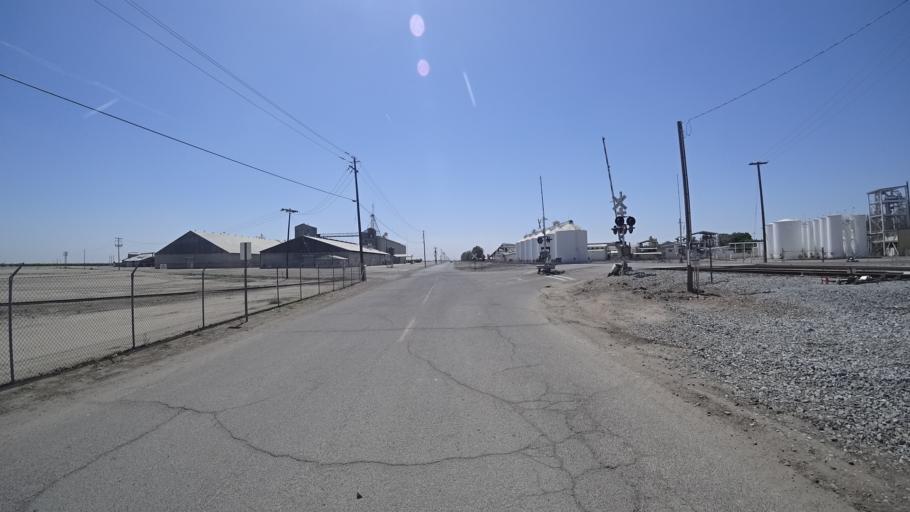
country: US
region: California
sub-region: Kings County
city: Corcoran
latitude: 36.0948
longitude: -119.5540
